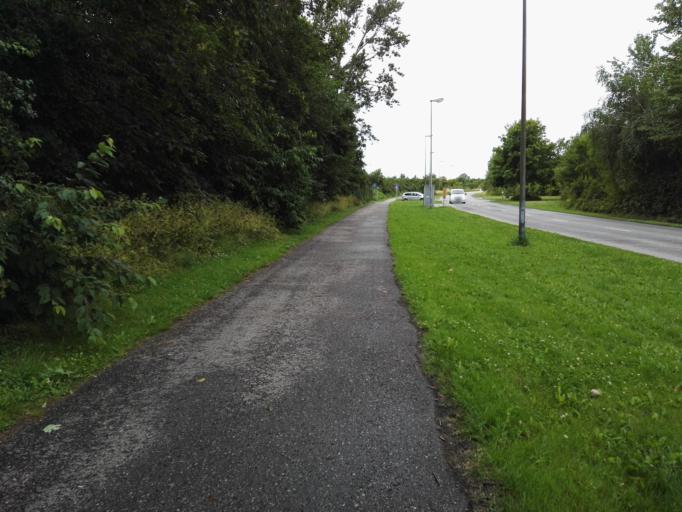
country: DK
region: Capital Region
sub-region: Egedal Kommune
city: Olstykke
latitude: 55.7736
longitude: 12.1637
